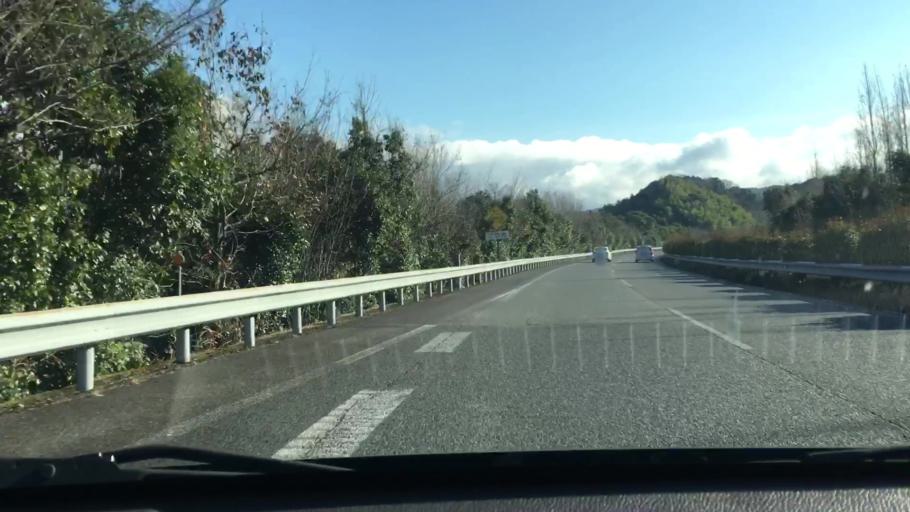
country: JP
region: Kumamoto
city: Hitoyoshi
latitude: 32.1973
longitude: 130.7774
